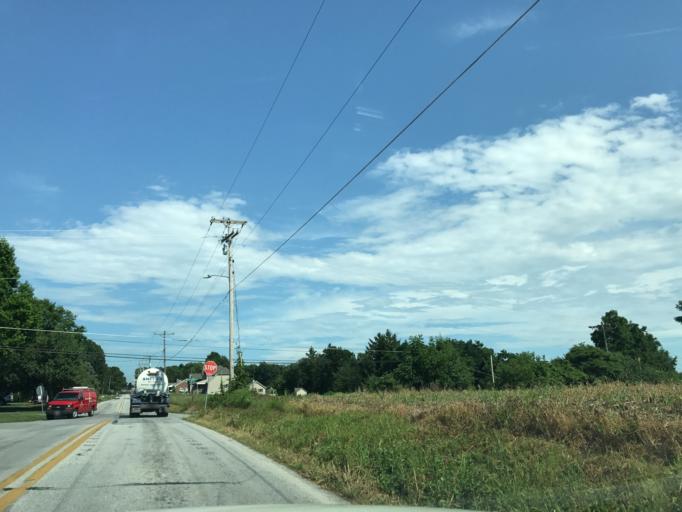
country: US
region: Pennsylvania
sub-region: York County
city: Pennville
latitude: 39.7624
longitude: -76.9940
